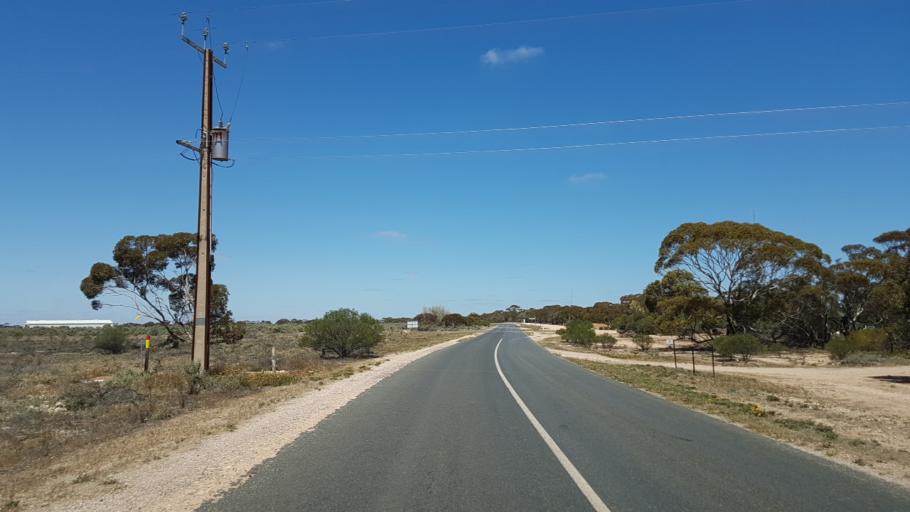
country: AU
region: South Australia
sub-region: Loxton Waikerie
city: Waikerie
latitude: -34.1815
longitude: 140.0239
